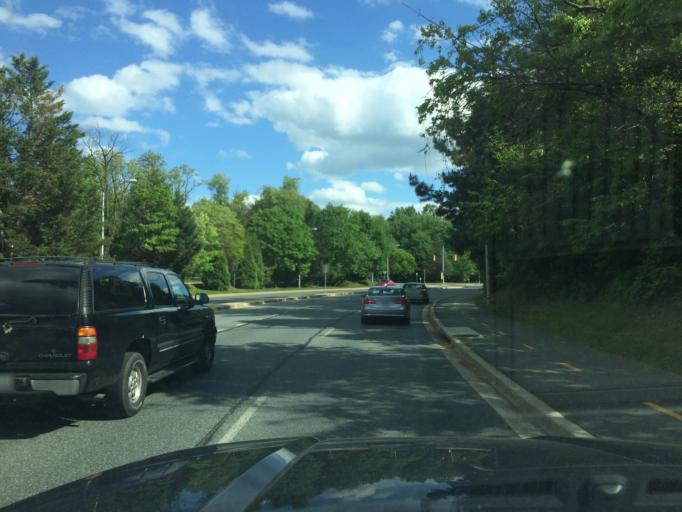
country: US
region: Maryland
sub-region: Montgomery County
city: Rockville
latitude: 39.0740
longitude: -77.1388
